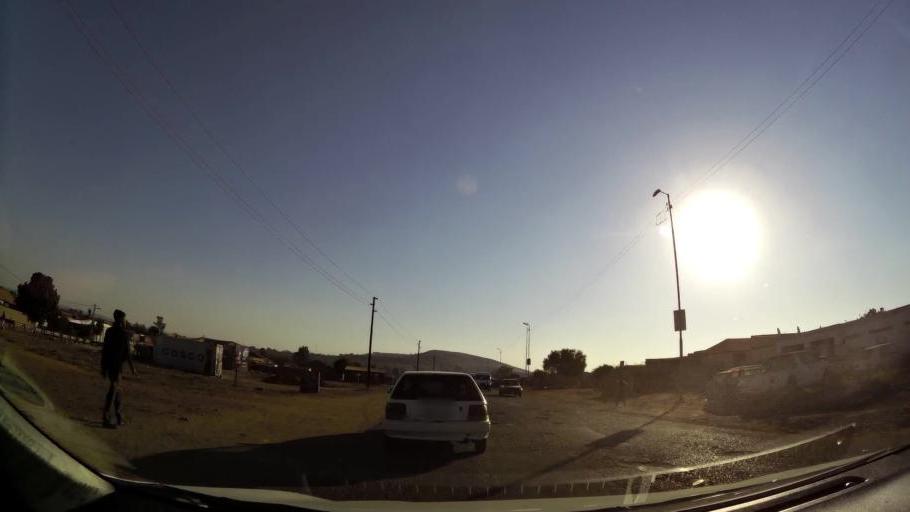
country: ZA
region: Gauteng
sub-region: City of Tshwane Metropolitan Municipality
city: Cullinan
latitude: -25.6977
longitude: 28.4108
